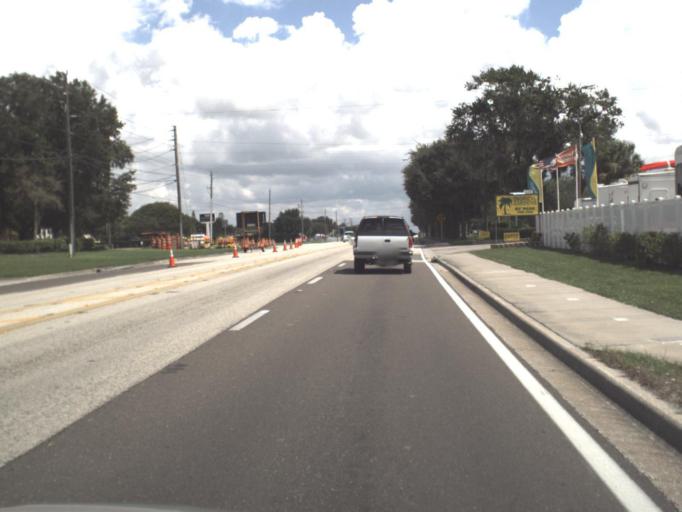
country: US
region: Florida
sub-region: Manatee County
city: West Samoset
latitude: 27.4477
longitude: -82.5517
